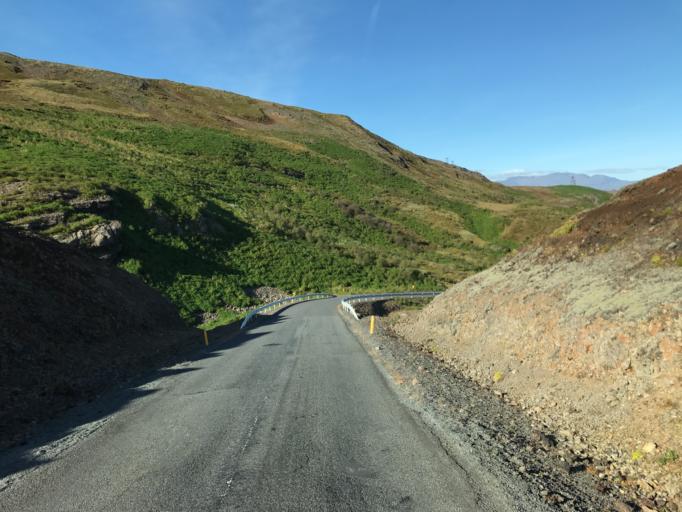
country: IS
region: South
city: Hveragerdi
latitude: 64.1186
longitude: -21.2613
